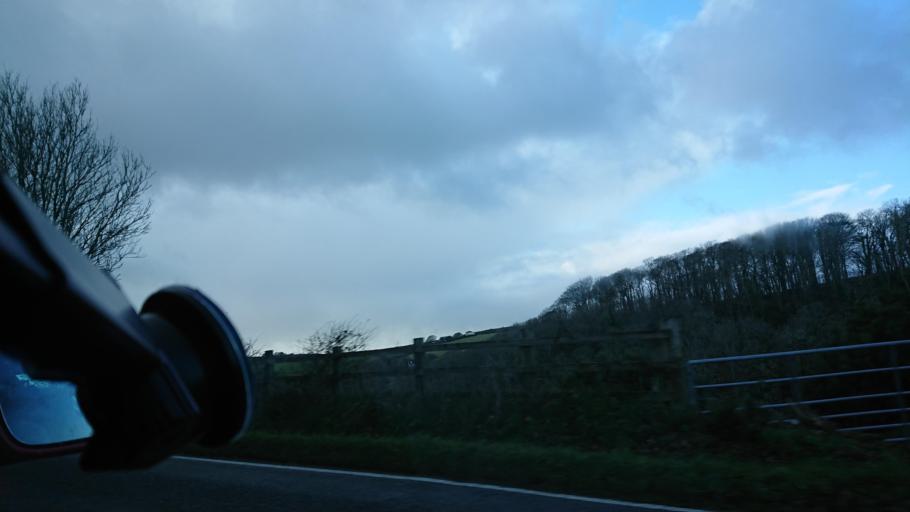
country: GB
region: England
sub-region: Cornwall
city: Looe
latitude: 50.3527
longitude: -4.4739
